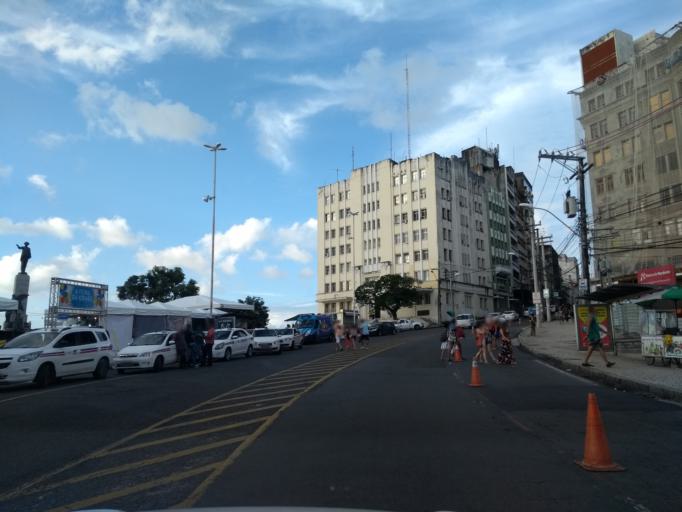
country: BR
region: Bahia
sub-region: Salvador
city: Salvador
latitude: -12.9773
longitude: -38.5146
